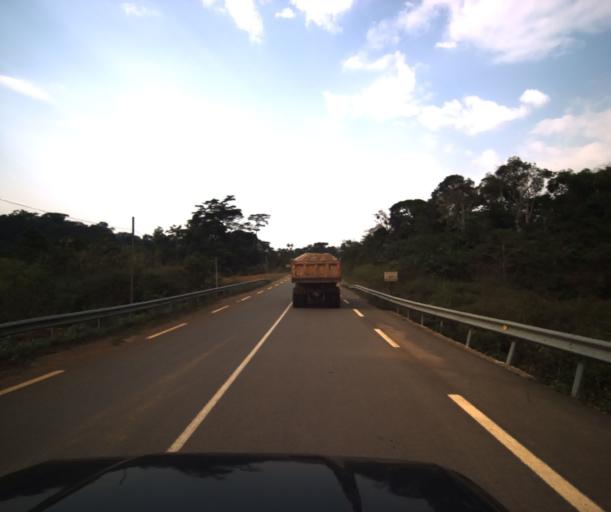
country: CM
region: Centre
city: Mbankomo
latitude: 3.6560
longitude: 11.3409
